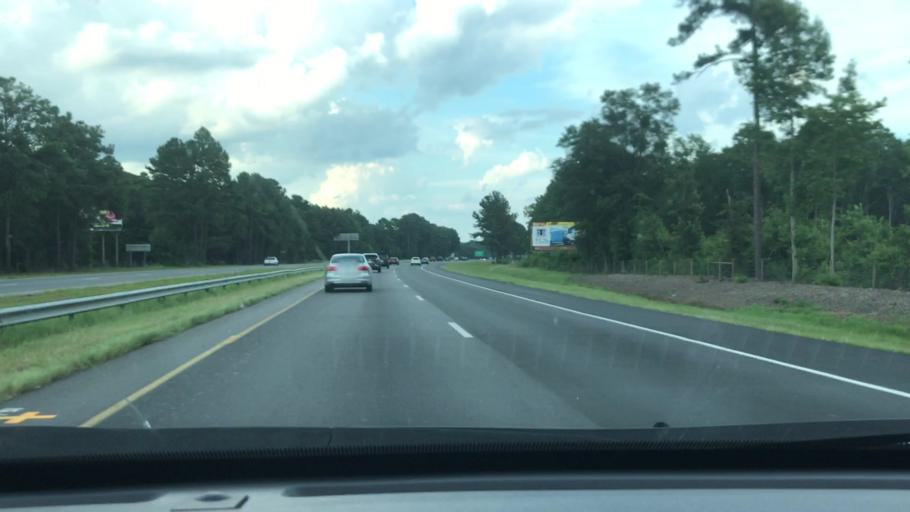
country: US
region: North Carolina
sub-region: Cumberland County
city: Eastover
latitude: 35.1101
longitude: -78.7674
